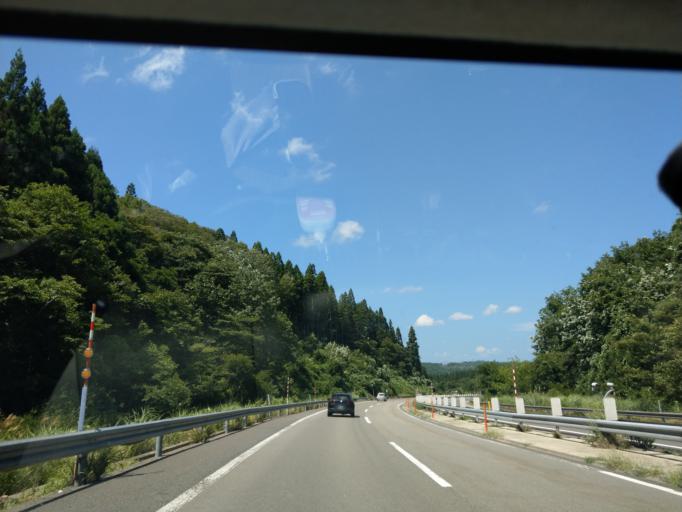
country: JP
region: Akita
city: Akita
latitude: 39.5822
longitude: 140.2890
